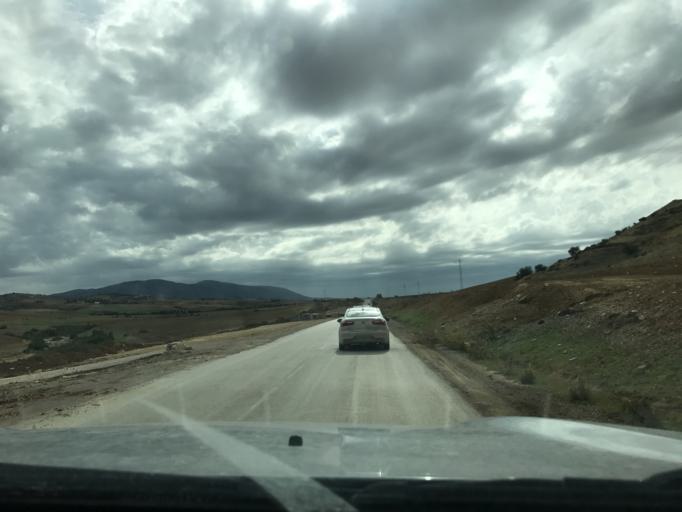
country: TN
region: Silyanah
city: Bu `Aradah
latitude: 36.1798
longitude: 9.6649
